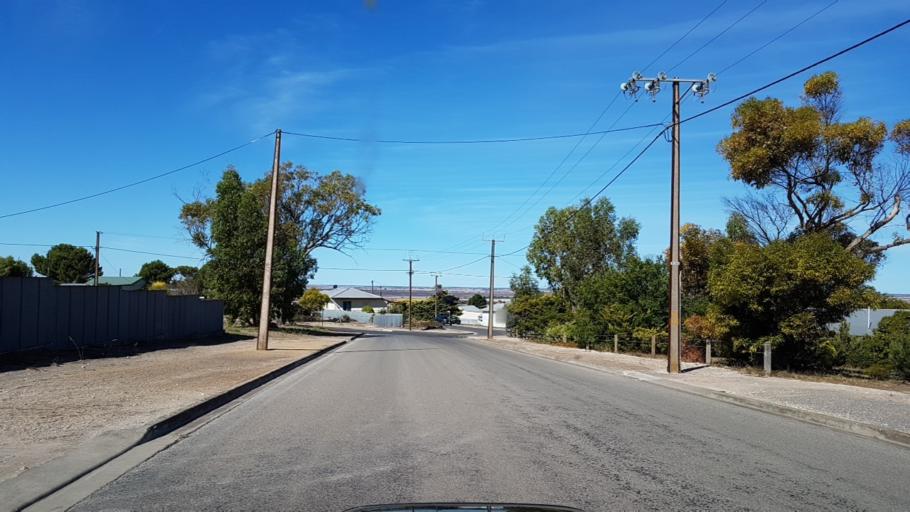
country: AU
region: South Australia
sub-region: Yorke Peninsula
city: Honiton
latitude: -34.9922
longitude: 137.4020
